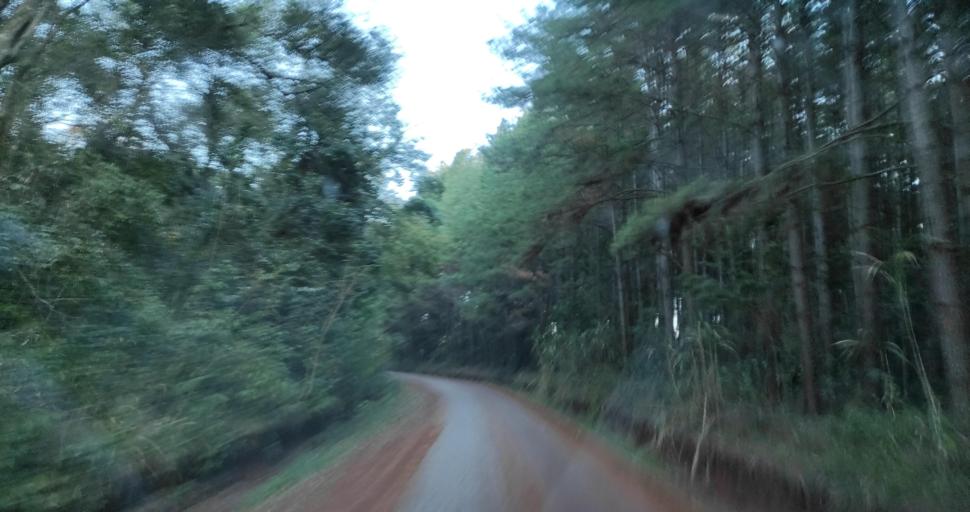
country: AR
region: Misiones
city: Capiovi
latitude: -26.8835
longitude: -55.0851
